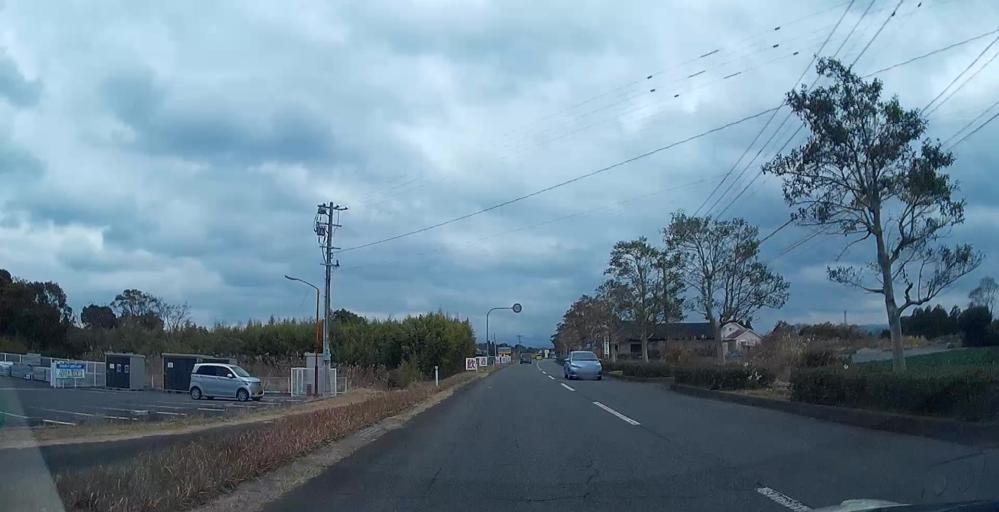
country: JP
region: Kagoshima
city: Akune
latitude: 32.0756
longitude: 130.2103
